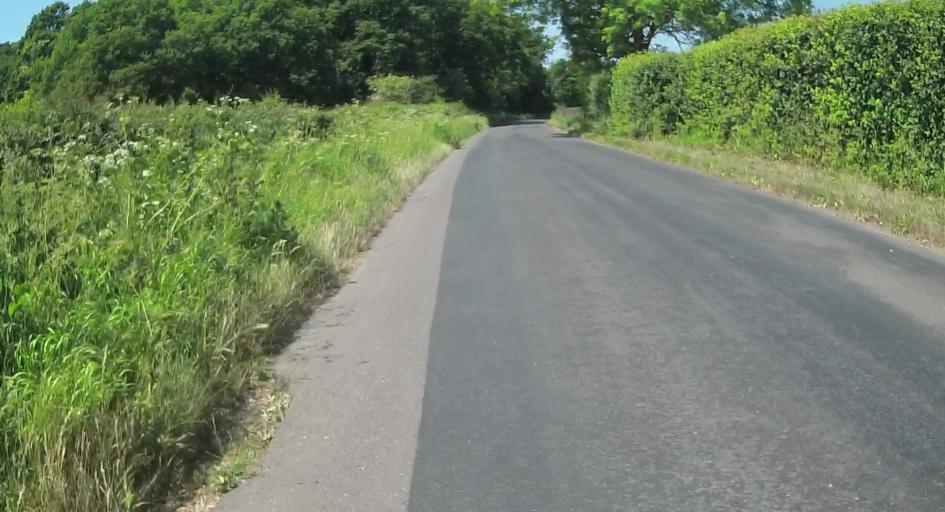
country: GB
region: England
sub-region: Hampshire
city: Tadley
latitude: 51.3220
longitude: -1.1712
